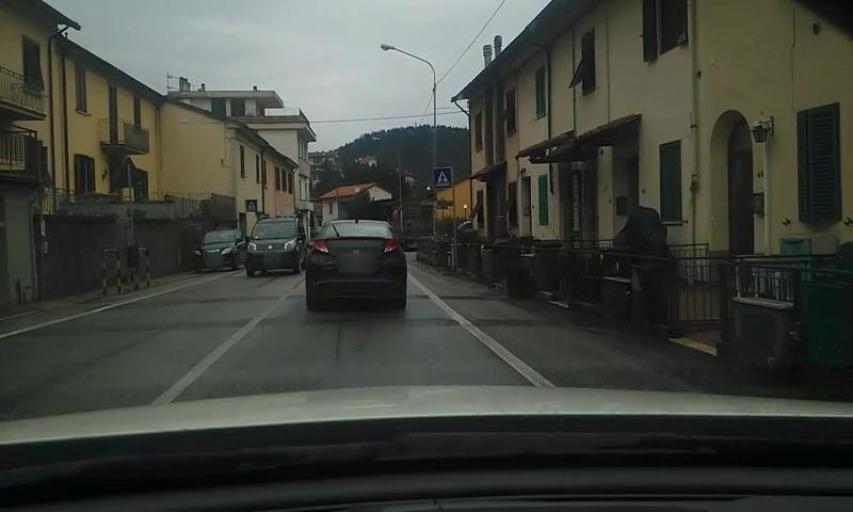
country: IT
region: Tuscany
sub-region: Provincia di Prato
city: Vaiano
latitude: 43.9355
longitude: 11.1254
